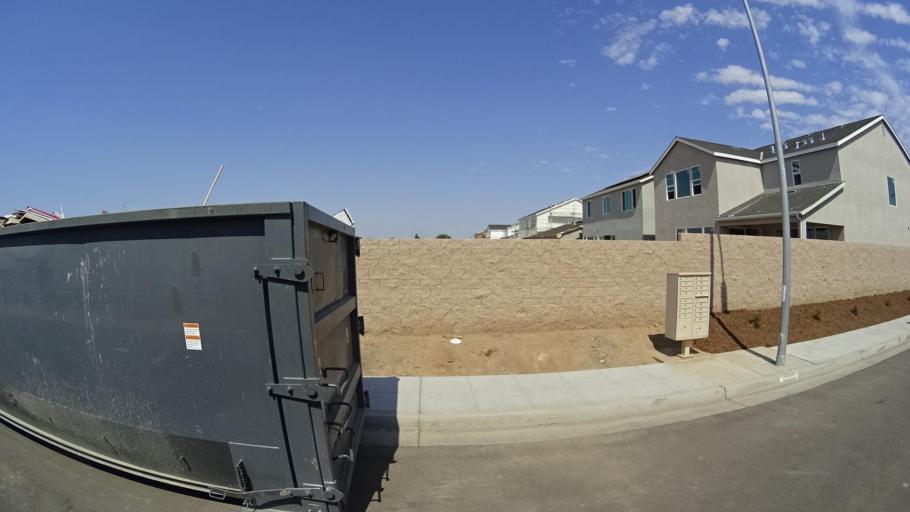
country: US
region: California
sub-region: Fresno County
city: Sunnyside
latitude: 36.7179
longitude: -119.6883
